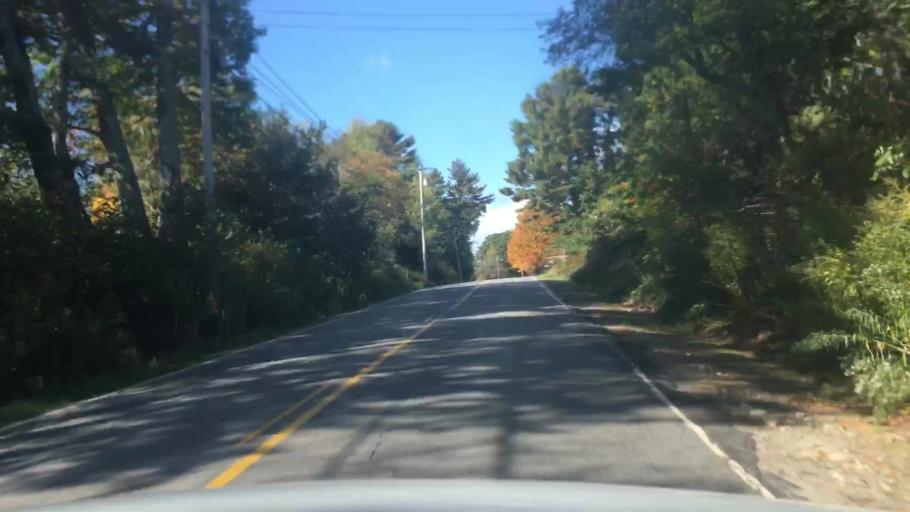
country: US
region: Maine
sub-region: Knox County
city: Thomaston
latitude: 44.0893
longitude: -69.2140
